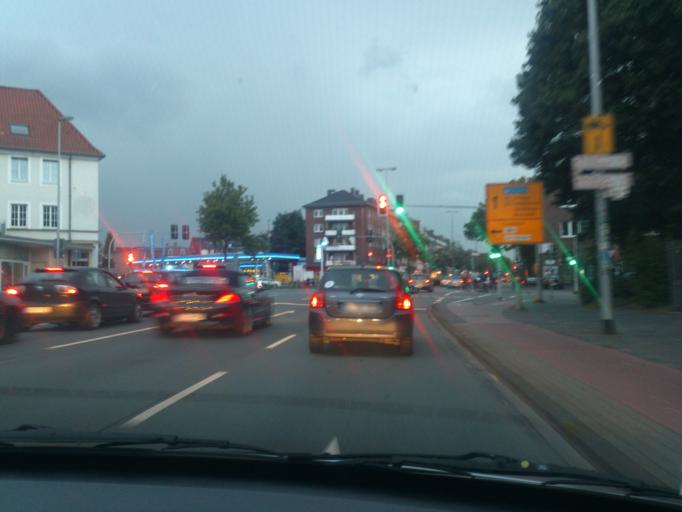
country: DE
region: North Rhine-Westphalia
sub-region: Regierungsbezirk Munster
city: Muenster
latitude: 51.9670
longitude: 7.6159
